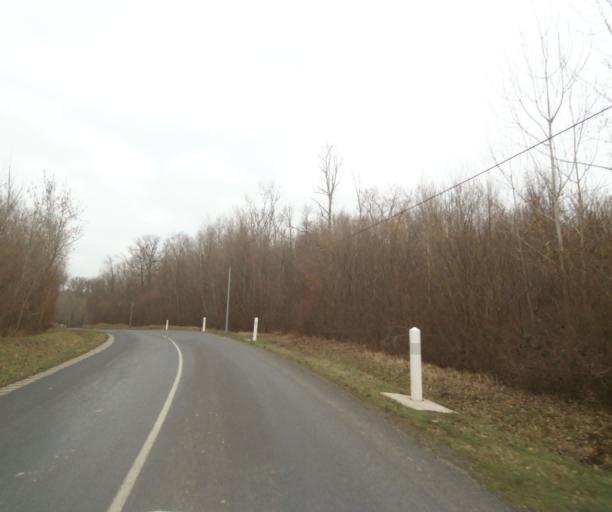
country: FR
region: Champagne-Ardenne
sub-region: Departement de la Haute-Marne
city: Villiers-en-Lieu
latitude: 48.6935
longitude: 4.8924
